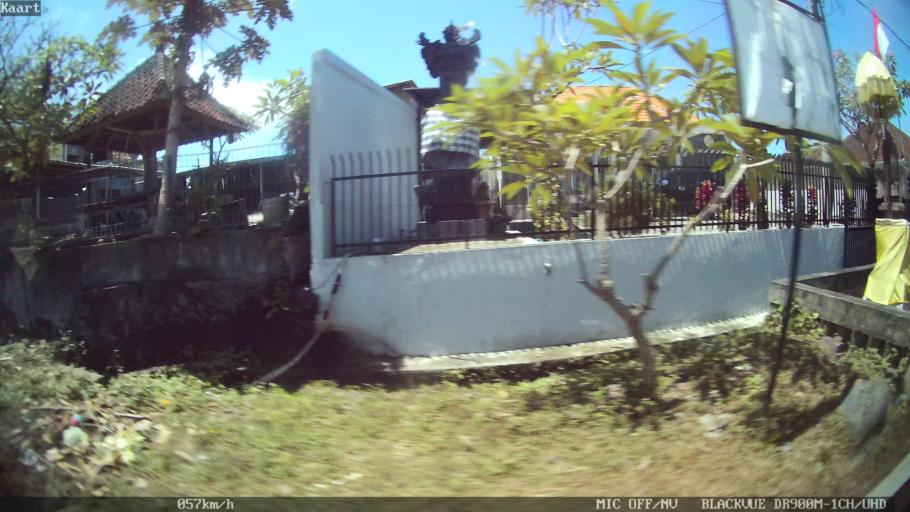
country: ID
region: Bali
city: Banjar Pasekan
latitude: -8.5667
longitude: 115.3205
